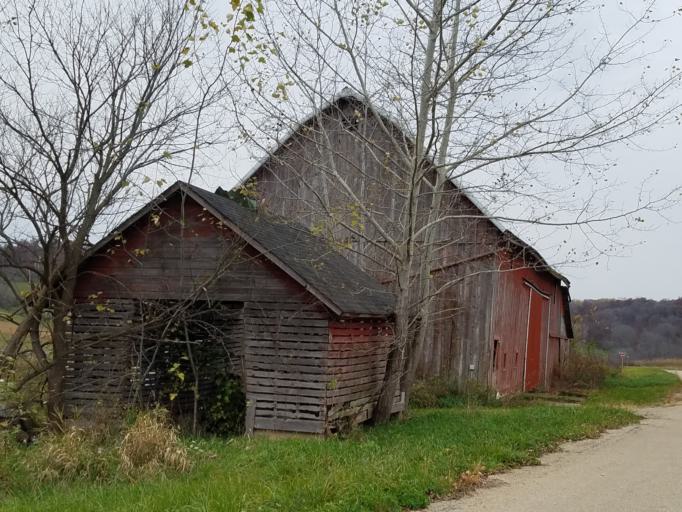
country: US
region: Wisconsin
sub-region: Vernon County
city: Hillsboro
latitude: 43.6095
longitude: -90.3507
